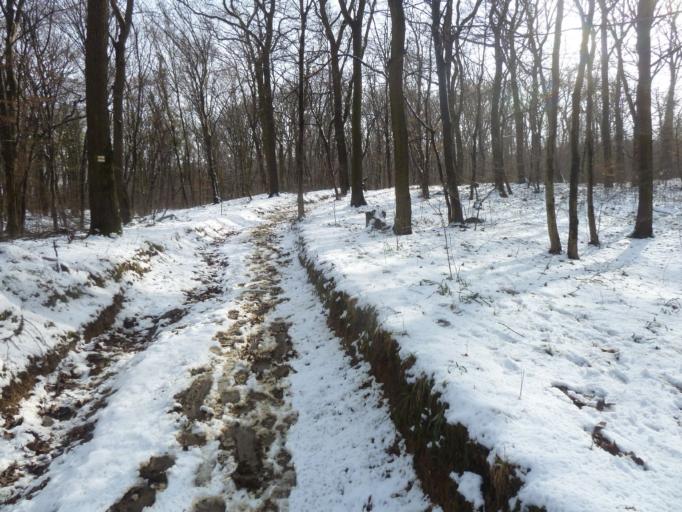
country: HU
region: Pest
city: Solymar
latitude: 47.5848
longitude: 18.9492
